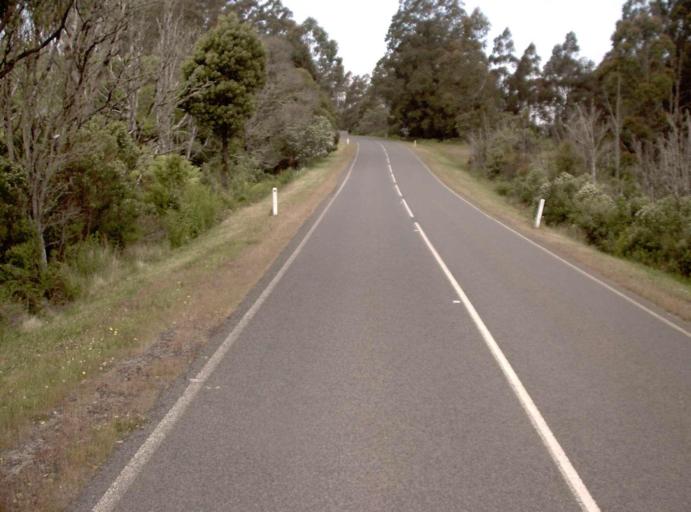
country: AU
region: Victoria
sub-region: Latrobe
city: Traralgon
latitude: -38.4047
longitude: 146.5643
